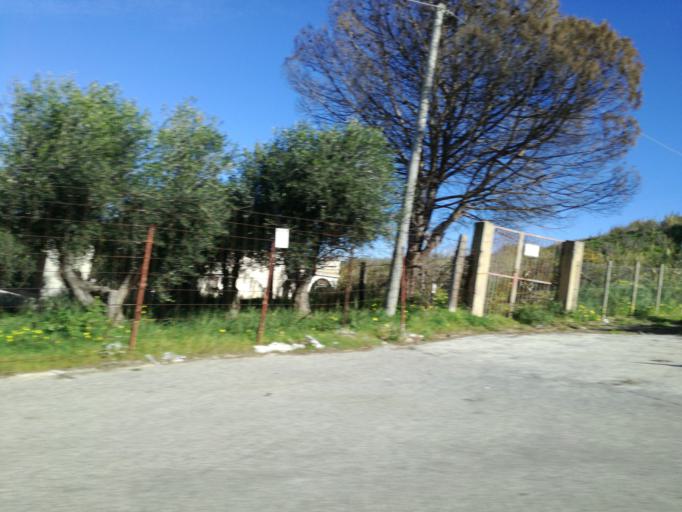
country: IT
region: Sicily
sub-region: Provincia di Caltanissetta
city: Gela
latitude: 37.0917
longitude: 14.1777
